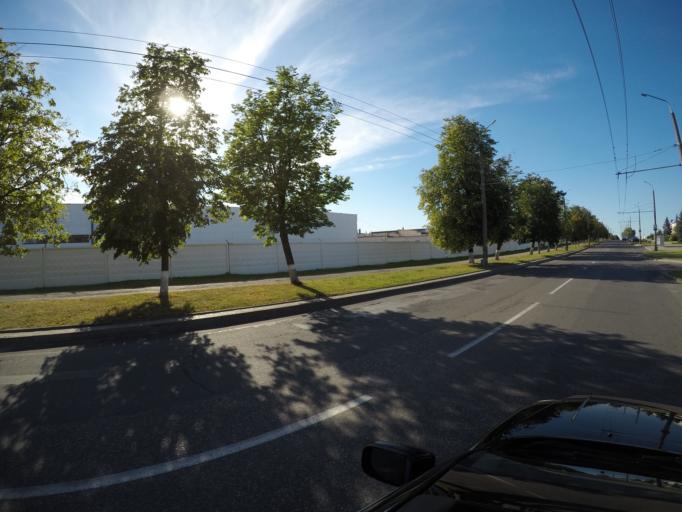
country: BY
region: Grodnenskaya
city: Hrodna
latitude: 53.7076
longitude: 23.8281
